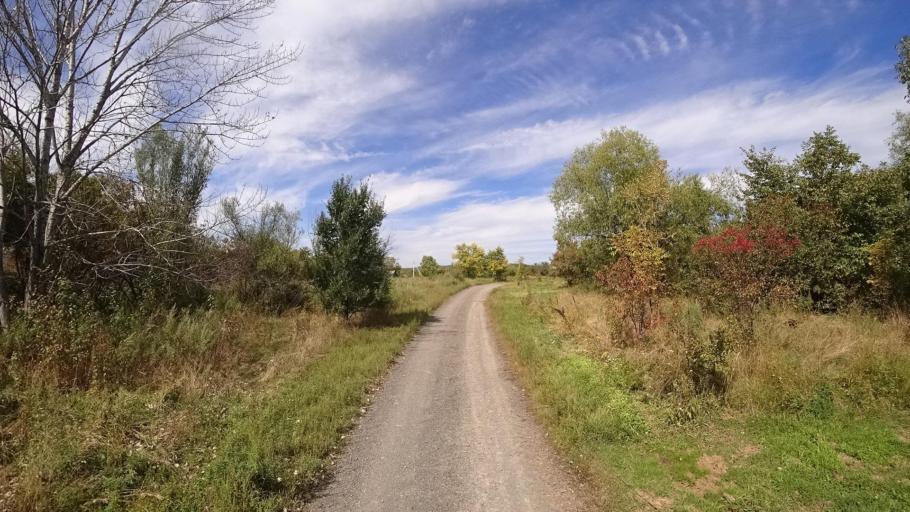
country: RU
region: Primorskiy
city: Yakovlevka
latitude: 44.6414
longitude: 133.5885
